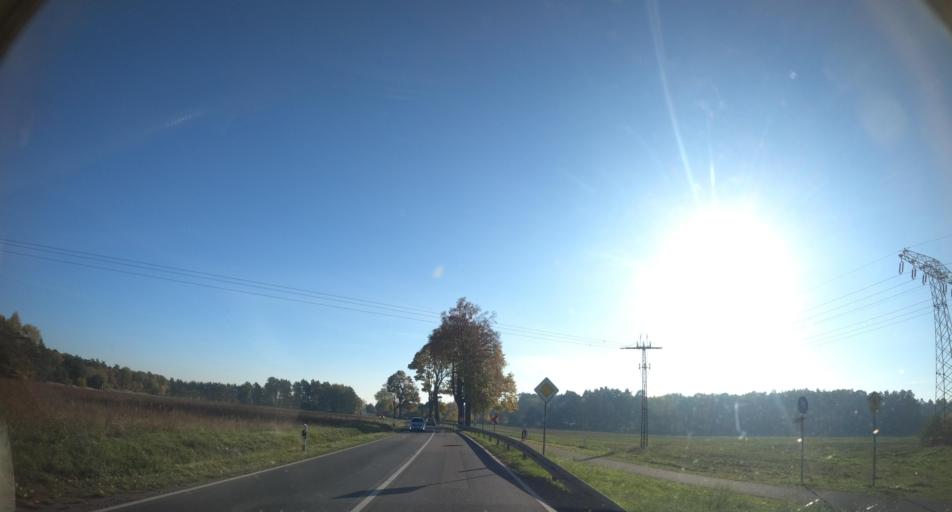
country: DE
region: Mecklenburg-Vorpommern
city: Ueckermunde
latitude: 53.7162
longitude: 14.0644
